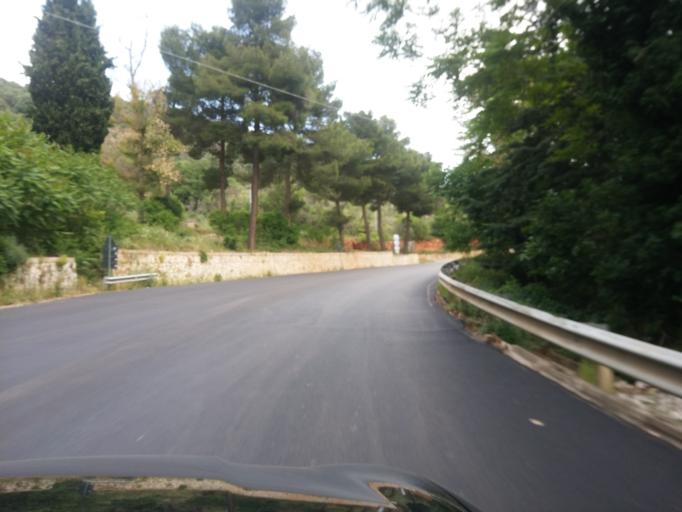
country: IT
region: Apulia
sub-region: Provincia di Foggia
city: Rignano Garganico
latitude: 41.7189
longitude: 15.5802
